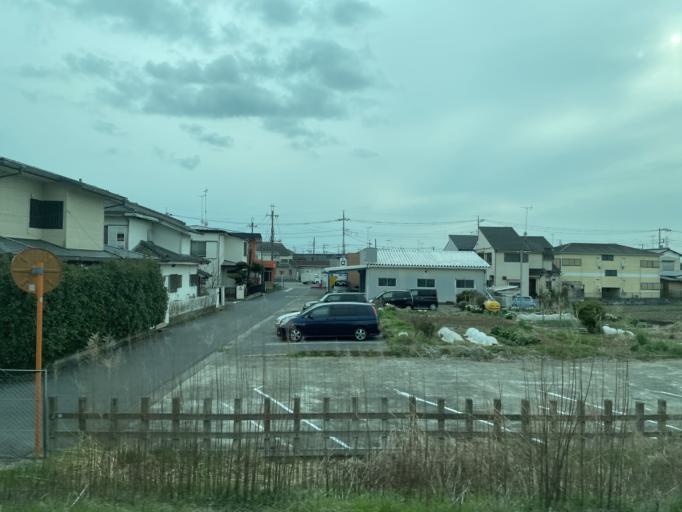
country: JP
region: Saitama
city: Sugito
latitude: 36.0431
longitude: 139.6966
